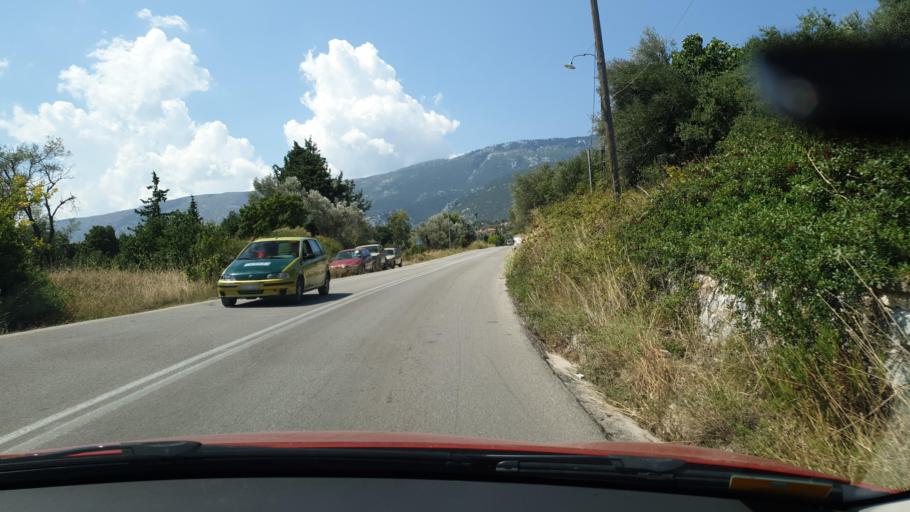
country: GR
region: Central Greece
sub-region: Nomos Evvoias
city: Oxilithos
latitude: 38.5837
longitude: 24.0636
